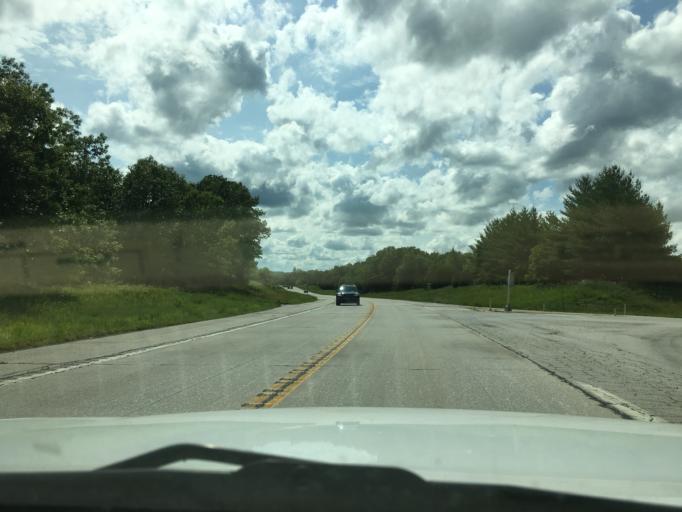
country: US
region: Missouri
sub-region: Franklin County
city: Gerald
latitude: 38.4235
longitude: -91.2622
